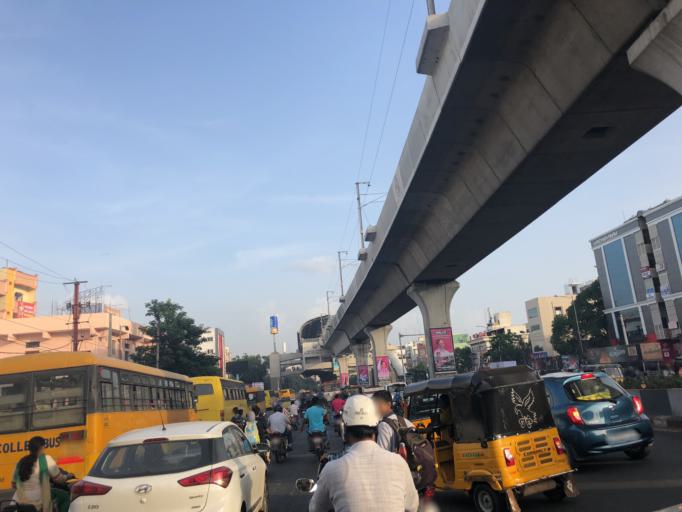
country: IN
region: Telangana
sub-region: Rangareddi
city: Kukatpalli
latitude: 17.4434
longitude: 78.4407
